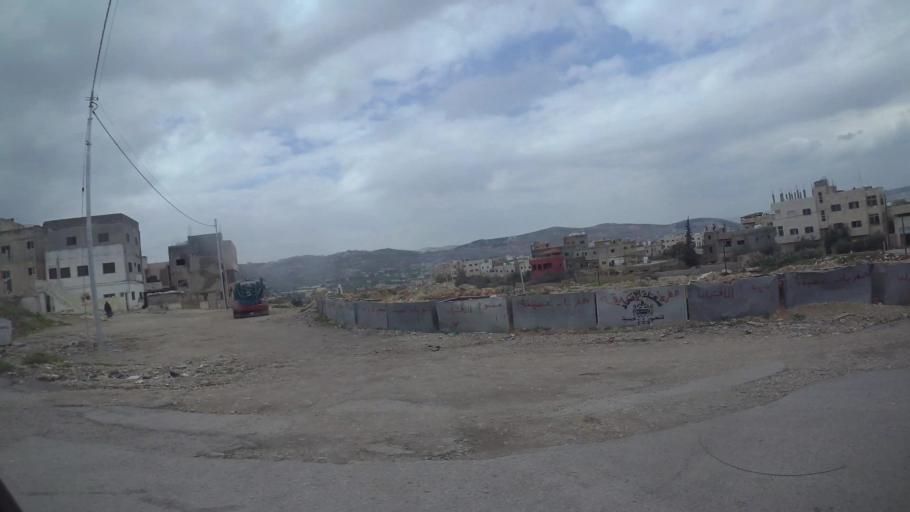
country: JO
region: Amman
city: Al Jubayhah
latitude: 32.0454
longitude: 35.8327
